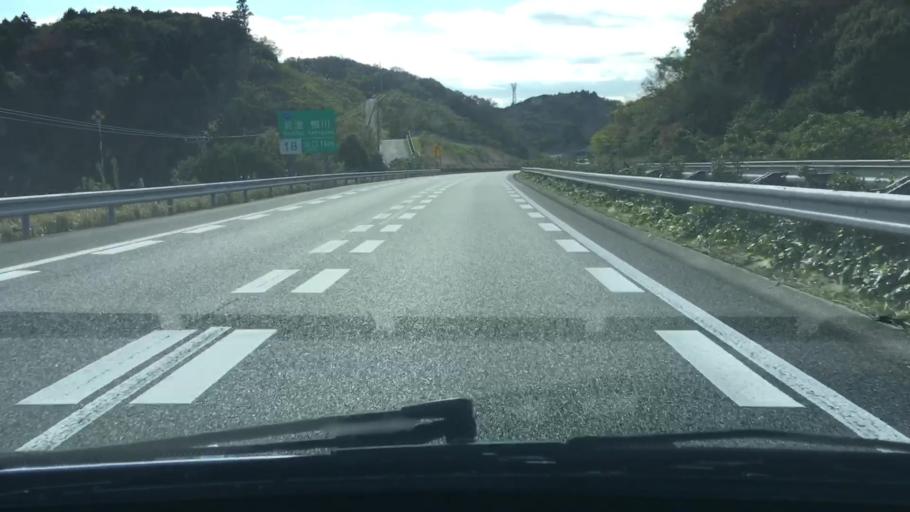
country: JP
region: Chiba
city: Kisarazu
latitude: 35.3304
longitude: 139.9461
